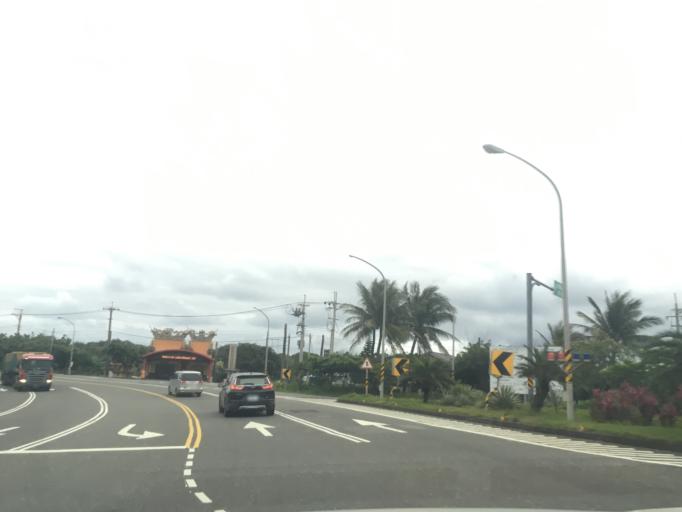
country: TW
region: Taiwan
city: Hengchun
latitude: 22.2948
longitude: 120.8879
